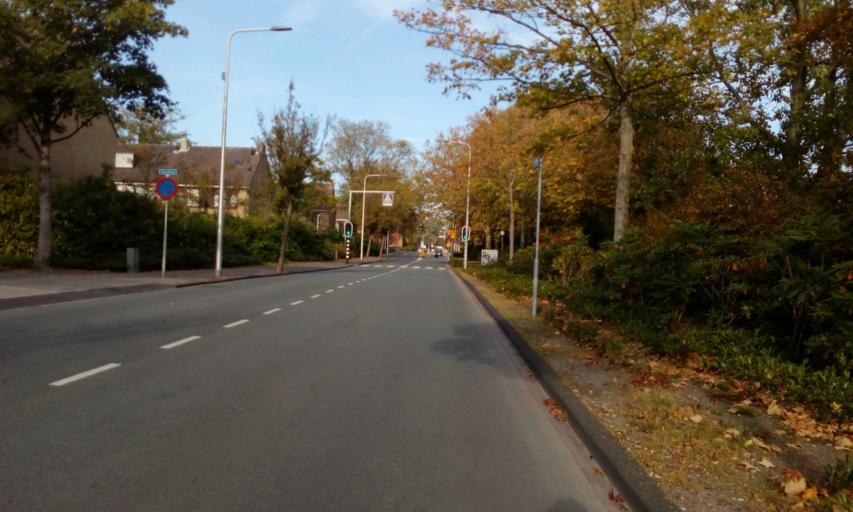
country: NL
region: South Holland
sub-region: Gemeente Westland
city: Naaldwijk
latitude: 51.9943
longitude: 4.2158
